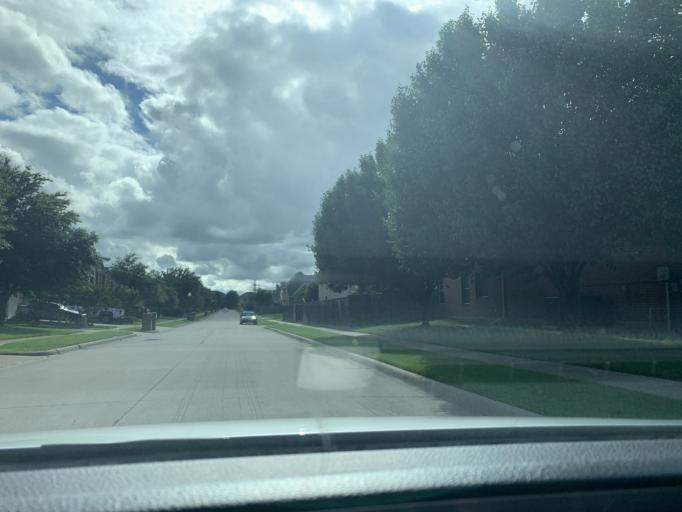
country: US
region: Texas
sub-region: Dallas County
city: Cedar Hill
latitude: 32.6400
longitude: -97.0438
